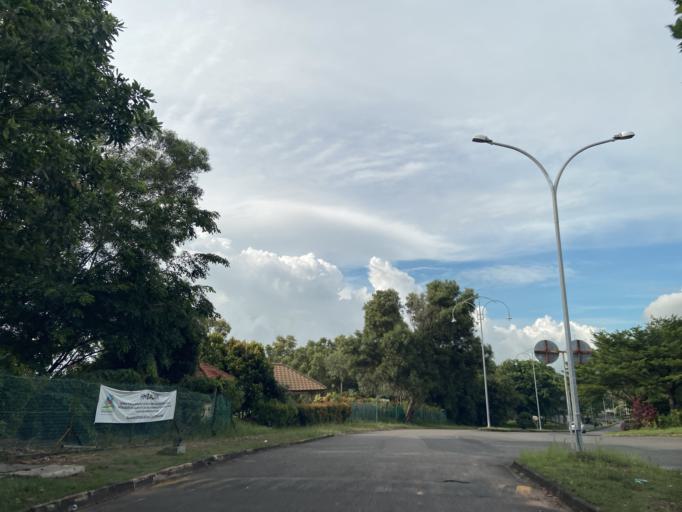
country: SG
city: Singapore
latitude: 1.0996
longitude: 104.0304
